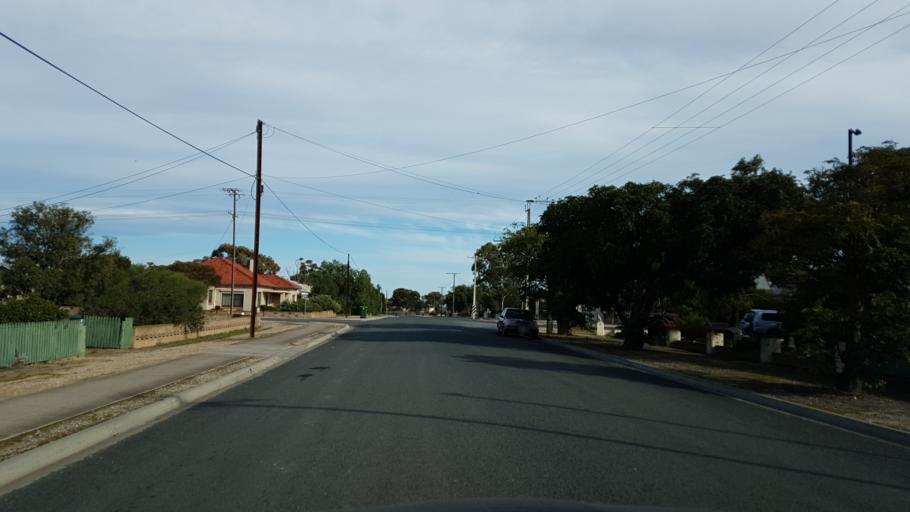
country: AU
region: South Australia
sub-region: Murray Bridge
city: Tailem Bend
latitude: -35.2517
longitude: 139.4584
